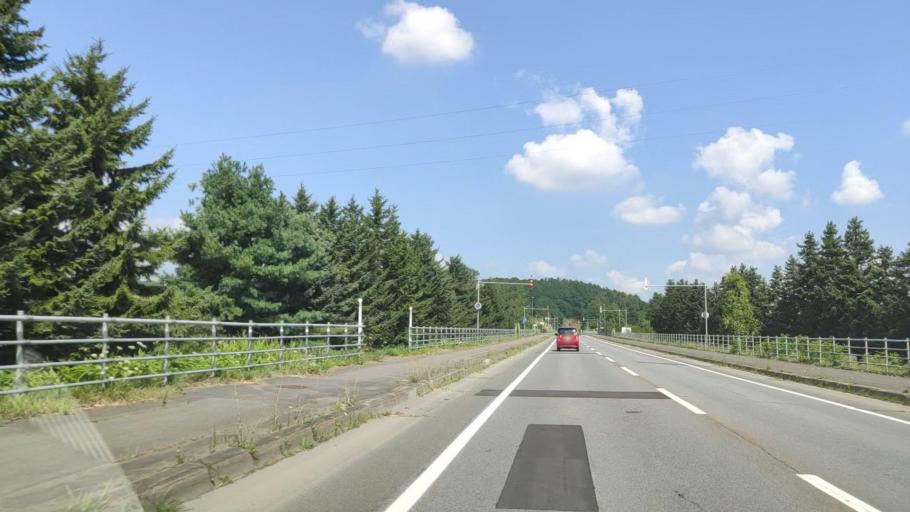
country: JP
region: Hokkaido
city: Shimo-furano
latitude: 43.4669
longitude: 142.4551
